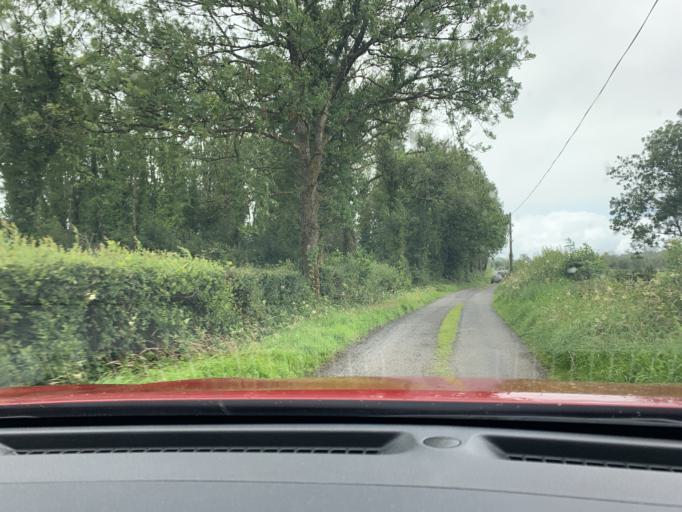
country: IE
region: Connaught
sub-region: County Leitrim
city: Carrick-on-Shannon
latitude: 53.8716
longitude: -8.1440
